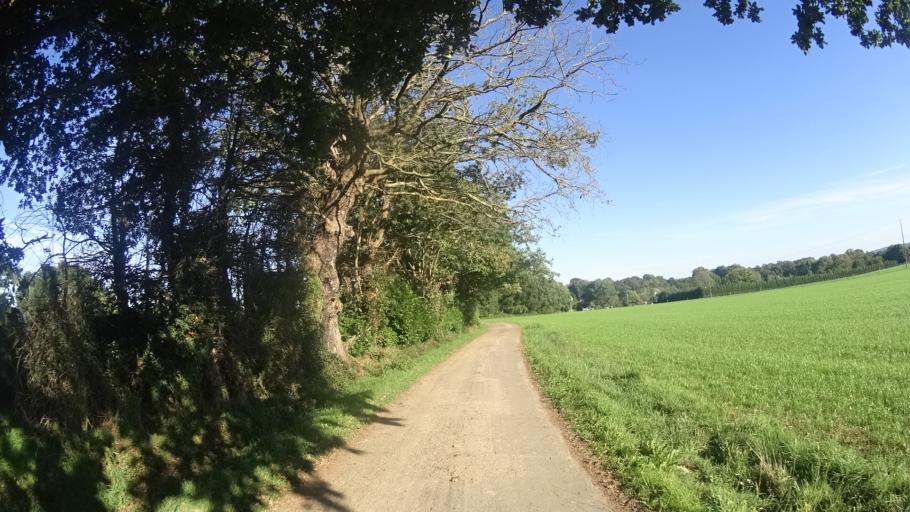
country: FR
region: Brittany
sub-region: Departement du Morbihan
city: Saint-Vincent-sur-Oust
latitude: 47.7071
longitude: -2.1750
